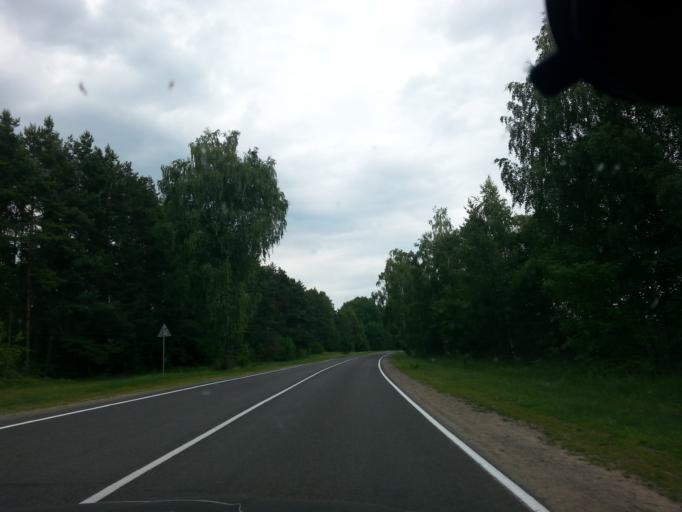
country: BY
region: Minsk
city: Narach
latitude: 54.9058
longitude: 26.7420
